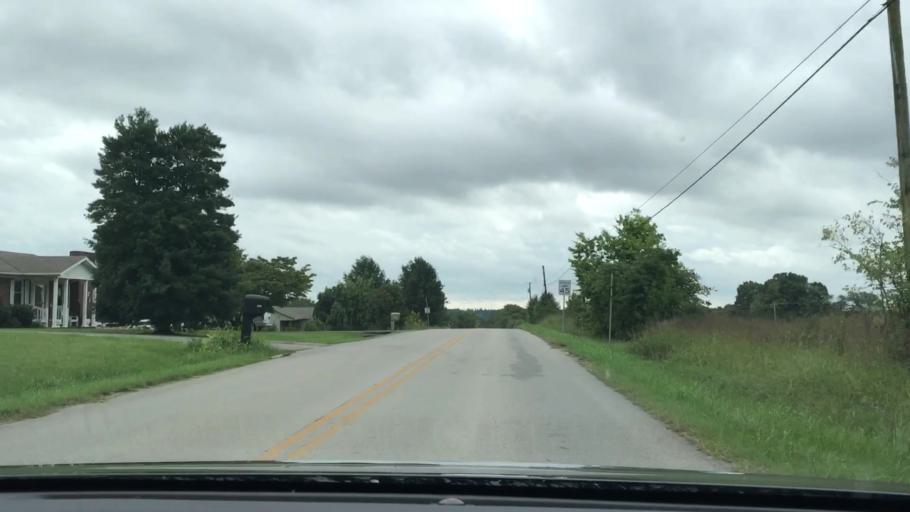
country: US
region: Kentucky
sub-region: Barren County
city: Glasgow
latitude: 36.9750
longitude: -85.8866
